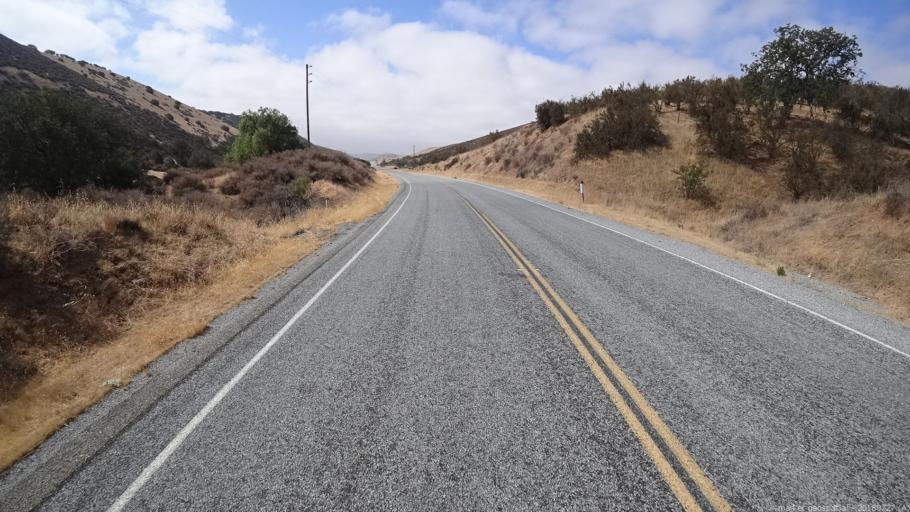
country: US
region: California
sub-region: Monterey County
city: King City
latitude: 36.2979
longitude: -121.0515
